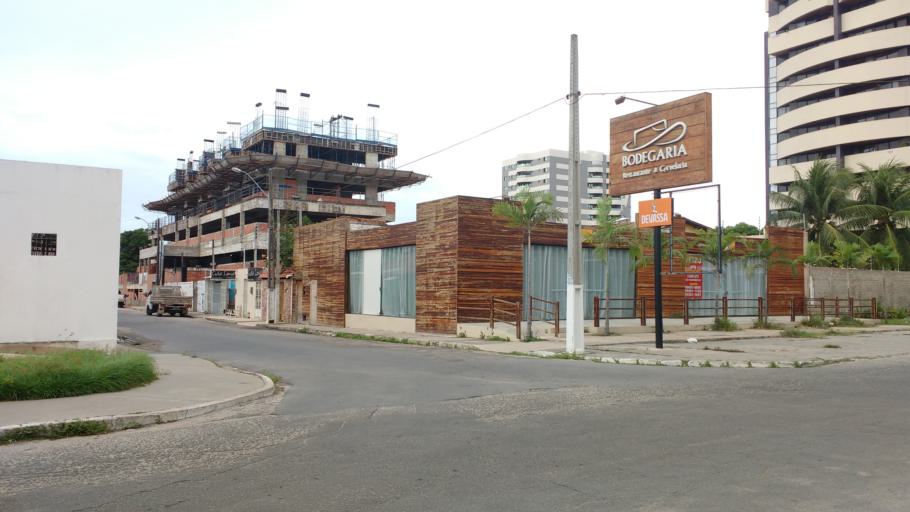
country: BR
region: Alagoas
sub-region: Maceio
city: Maceio
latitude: -9.6493
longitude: -35.7019
